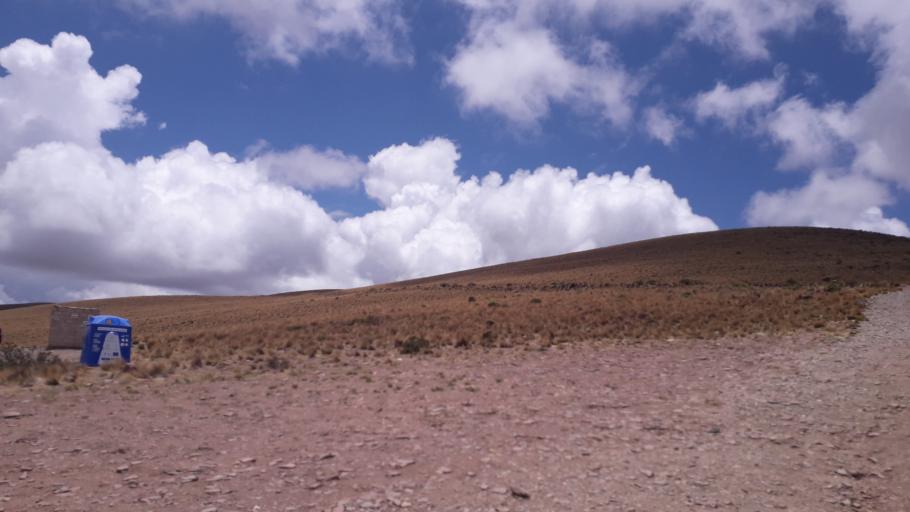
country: AR
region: Jujuy
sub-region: Departamento de Humahuaca
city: Humahuaca
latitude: -23.1972
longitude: -65.1935
